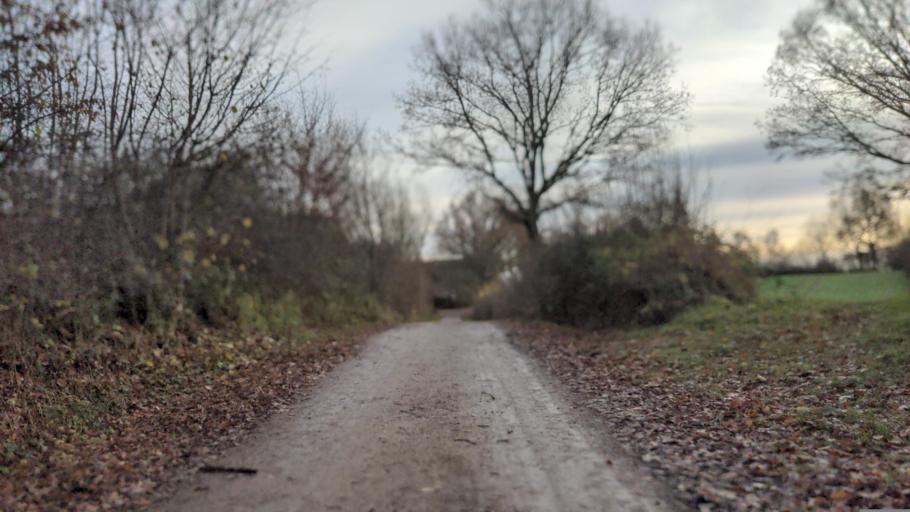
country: DE
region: Schleswig-Holstein
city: Neustadt in Holstein
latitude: 54.0901
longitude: 10.7927
